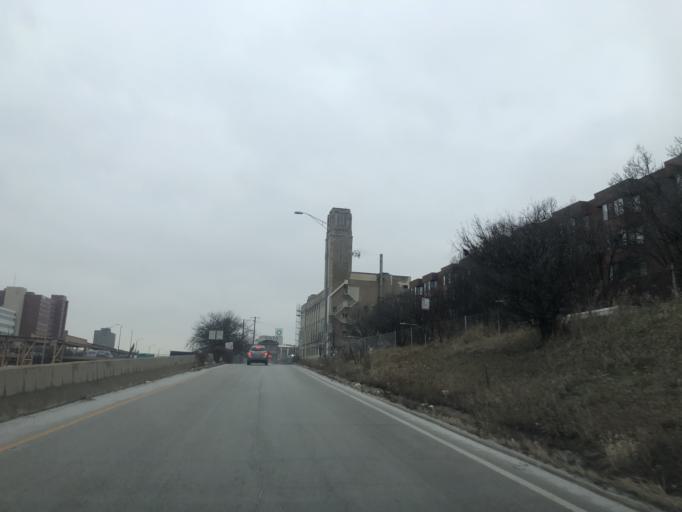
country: US
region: Illinois
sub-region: Cook County
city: Chicago
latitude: 41.8763
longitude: -87.6642
